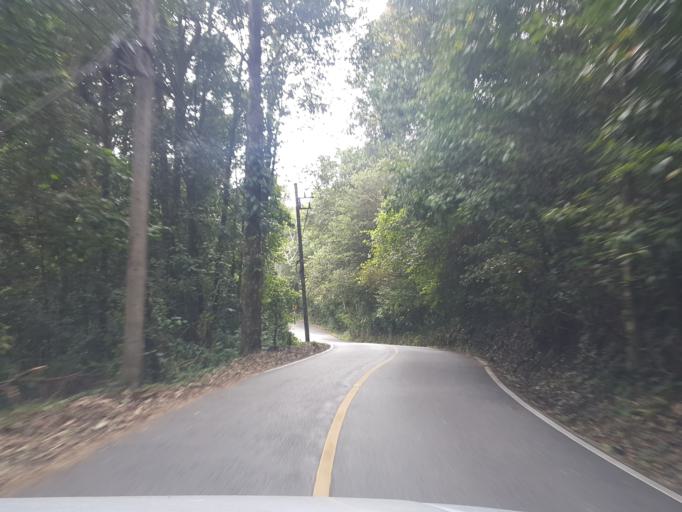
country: TH
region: Chiang Mai
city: Mae Chaem
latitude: 18.5264
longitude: 98.4941
